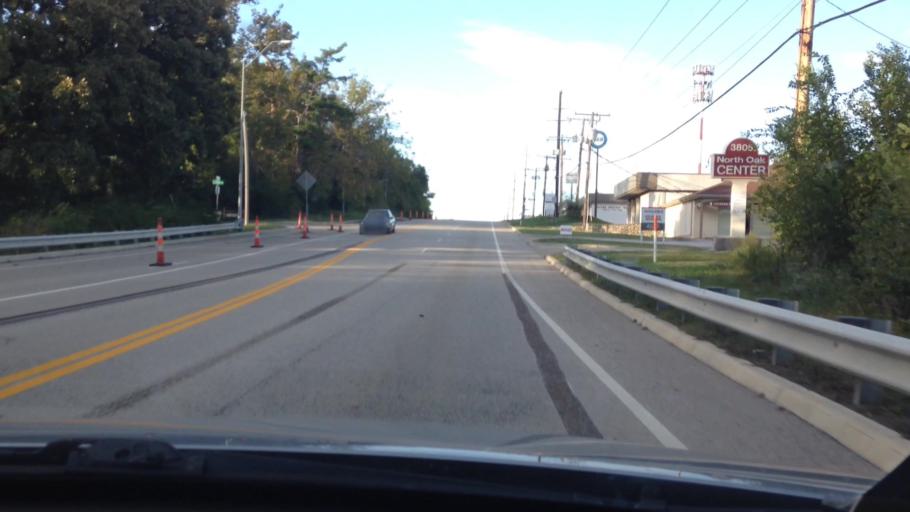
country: US
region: Missouri
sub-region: Clay County
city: North Kansas City
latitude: 39.1635
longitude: -94.5768
